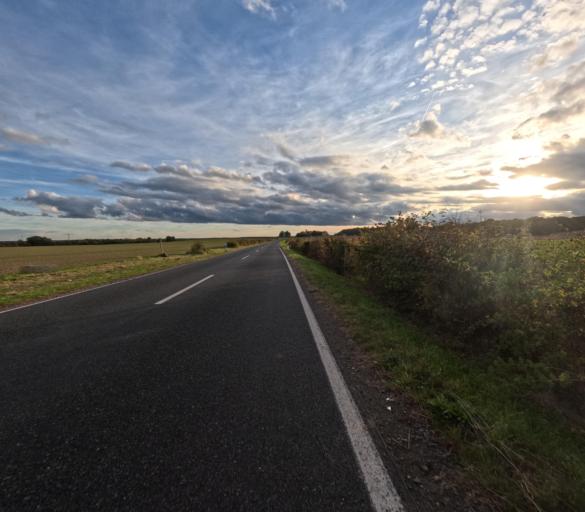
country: DE
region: Saxony
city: Grimma
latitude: 51.2538
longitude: 12.6795
